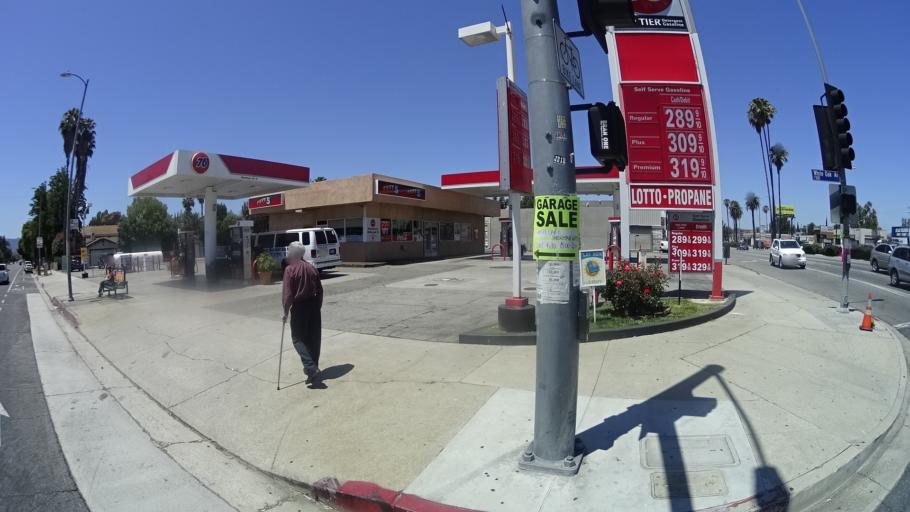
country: US
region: California
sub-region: Los Angeles County
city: Northridge
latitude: 34.2008
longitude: -118.5188
